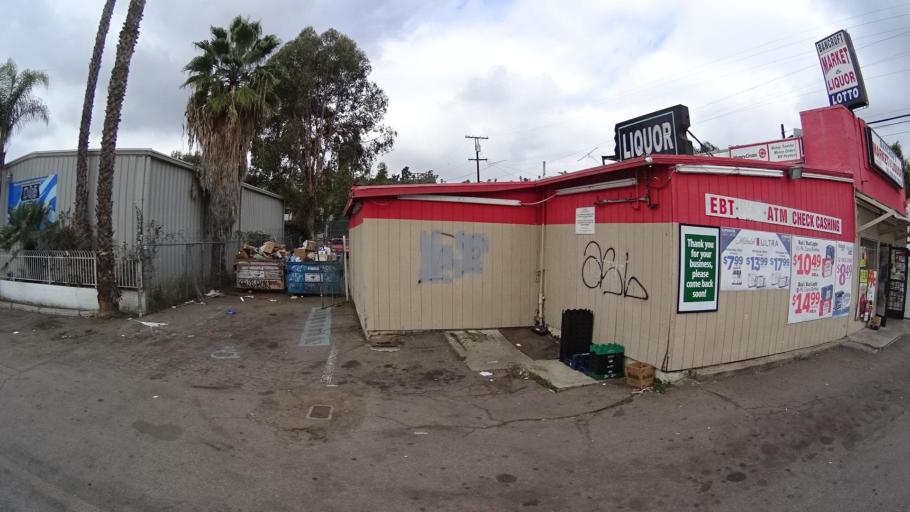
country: US
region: California
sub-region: San Diego County
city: Spring Valley
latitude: 32.7464
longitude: -117.0032
